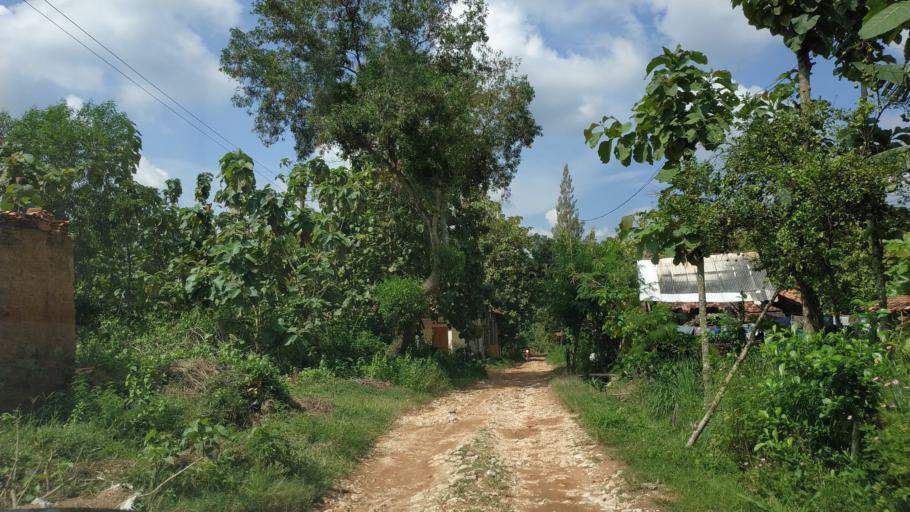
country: ID
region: Central Java
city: Guyangan
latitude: -7.0061
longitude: 111.1024
